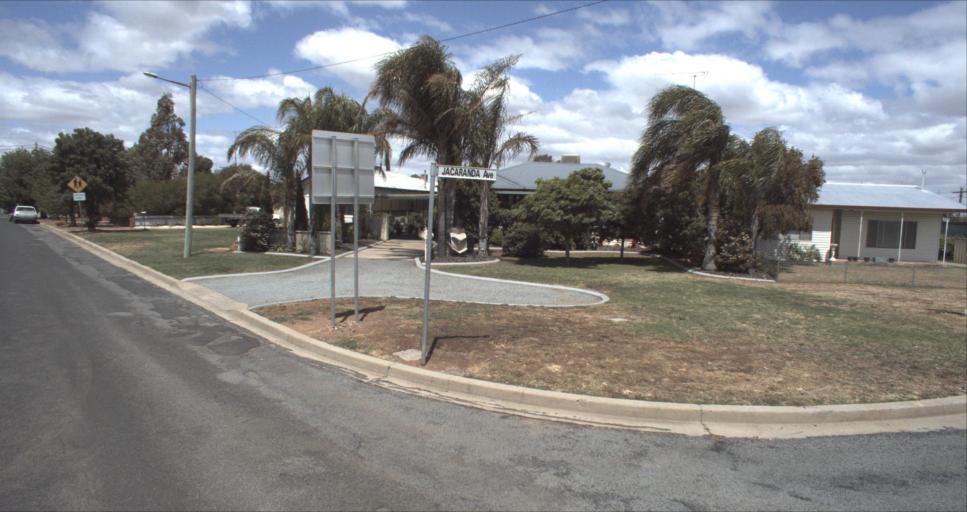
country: AU
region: New South Wales
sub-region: Leeton
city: Leeton
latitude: -34.5618
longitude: 146.3952
